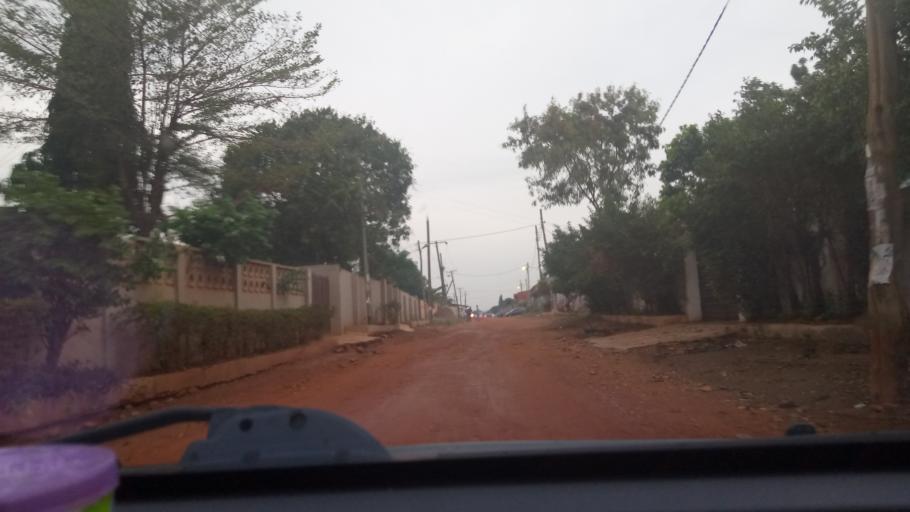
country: GH
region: Greater Accra
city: Medina Estates
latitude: 5.7040
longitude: -0.1671
